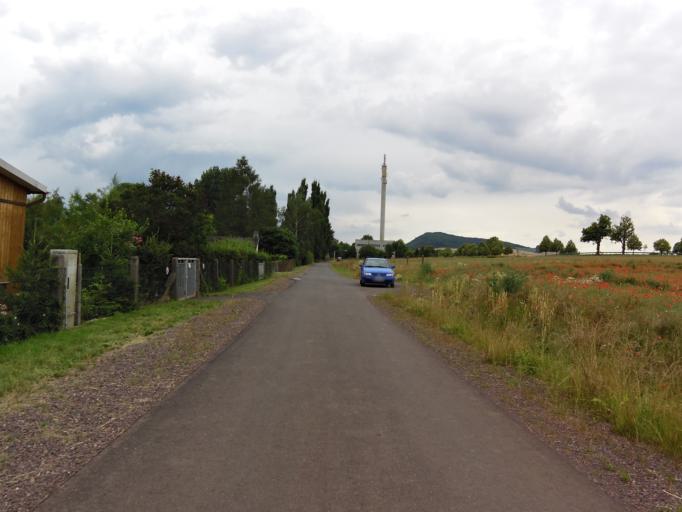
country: DE
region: Thuringia
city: Mechterstadt
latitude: 50.9423
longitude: 10.5121
